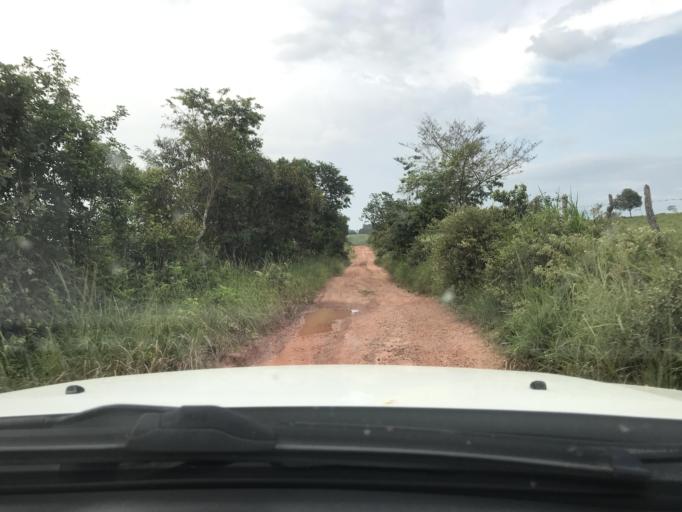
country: BR
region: Bahia
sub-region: Entre Rios
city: Entre Rios
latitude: -12.0155
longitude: -38.2216
